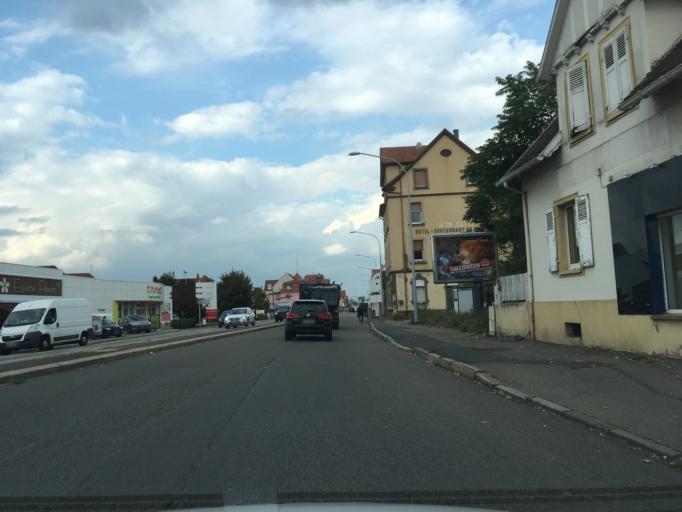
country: FR
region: Alsace
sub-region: Departement du Haut-Rhin
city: Colmar
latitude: 48.0886
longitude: 7.3599
